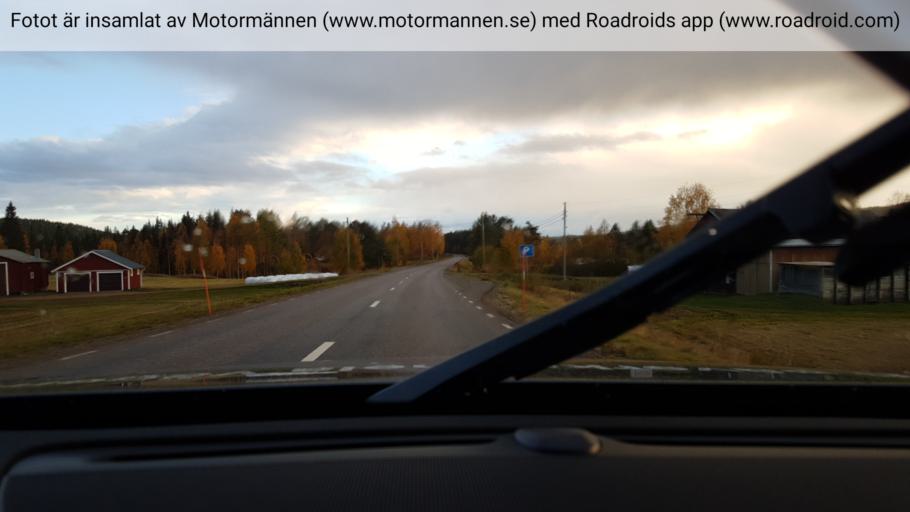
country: SE
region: Norrbotten
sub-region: Overkalix Kommun
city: OEverkalix
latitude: 66.5142
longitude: 22.7661
